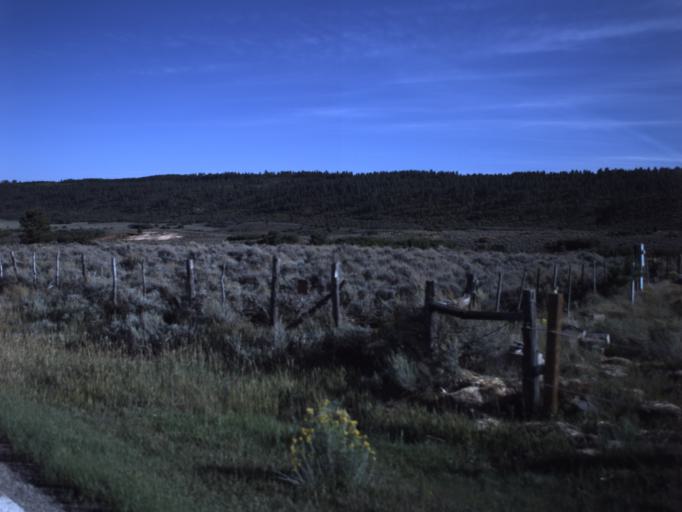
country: US
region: Utah
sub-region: Grand County
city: Moab
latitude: 38.3375
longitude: -109.1630
